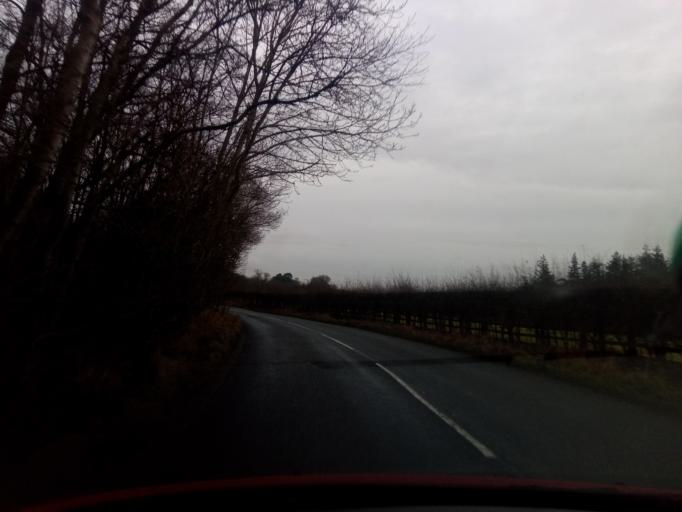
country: GB
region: England
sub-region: Northumberland
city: Rochester
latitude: 55.1658
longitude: -2.3987
